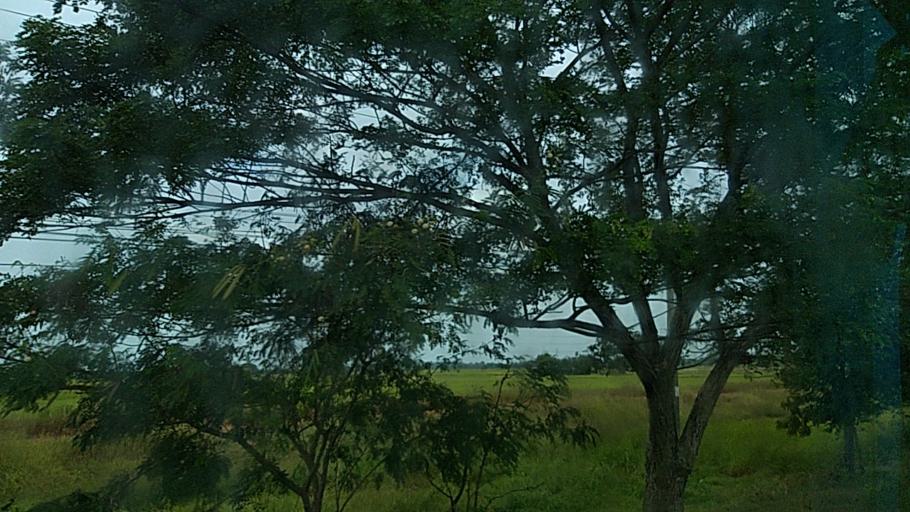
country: TH
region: Roi Et
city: Si Somdet
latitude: 16.1241
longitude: 103.4778
